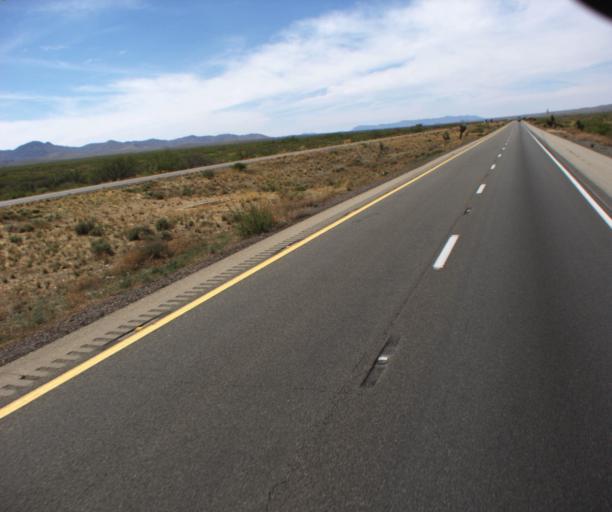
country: US
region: Arizona
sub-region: Cochise County
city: Willcox
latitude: 32.3404
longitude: -109.5614
